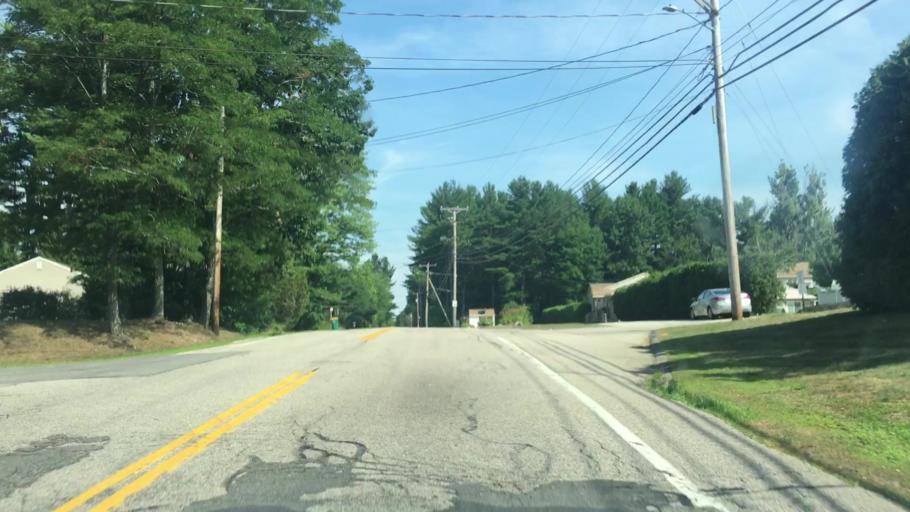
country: US
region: New Hampshire
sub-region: Strafford County
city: Rochester
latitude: 43.2822
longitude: -70.9727
